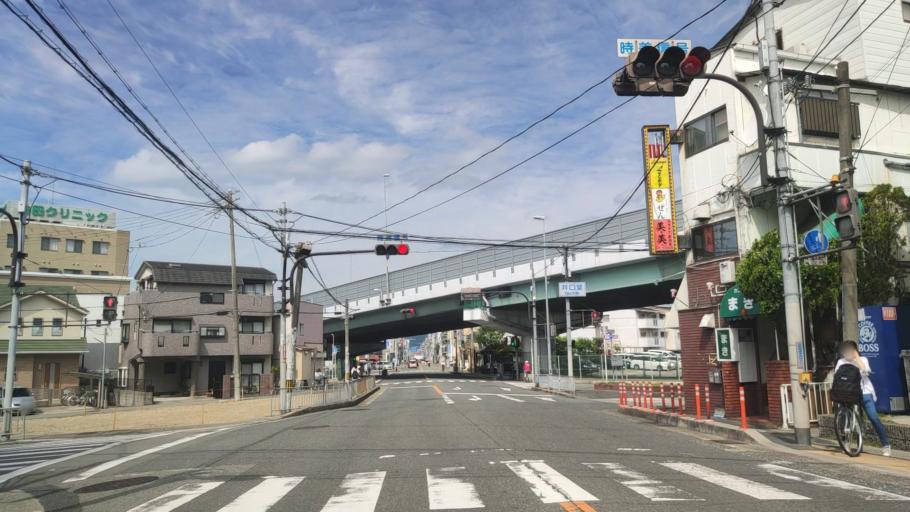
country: JP
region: Osaka
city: Ikeda
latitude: 34.8104
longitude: 135.4445
